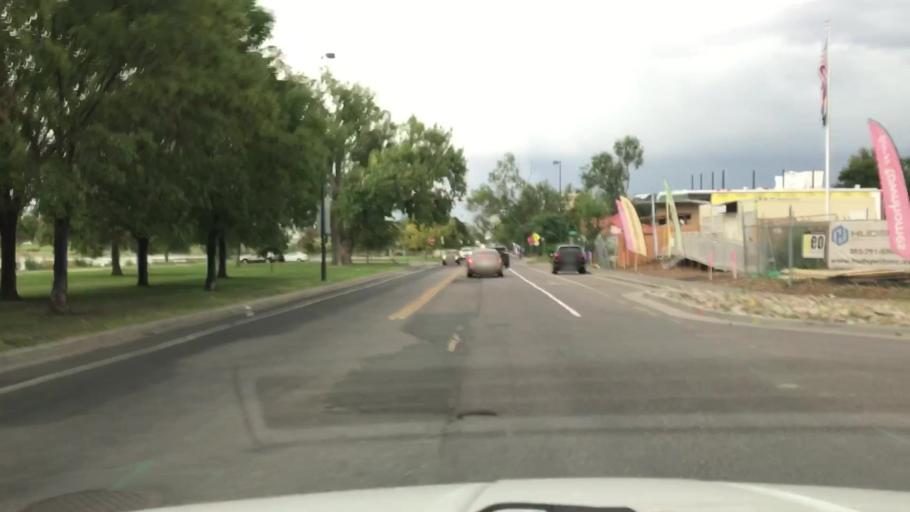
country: US
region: Colorado
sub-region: Jefferson County
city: Edgewater
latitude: 39.7439
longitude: -105.0408
